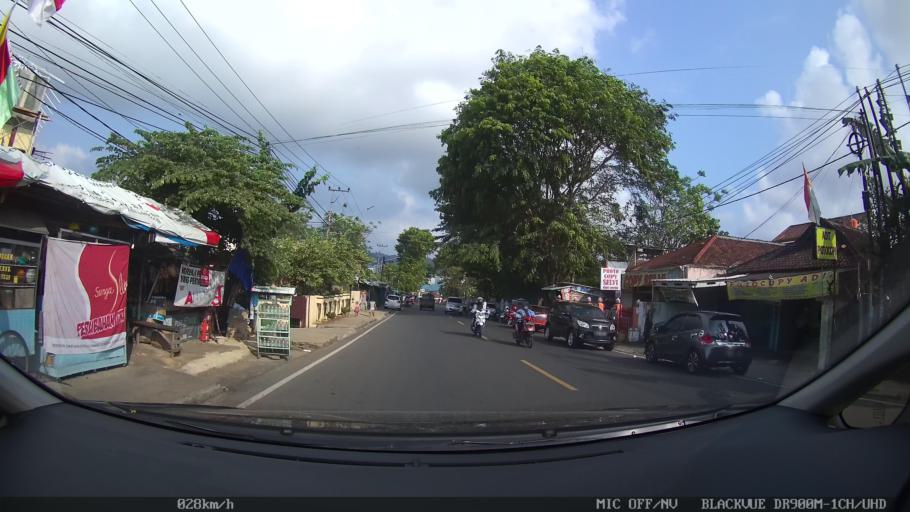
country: ID
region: Lampung
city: Bandarlampung
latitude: -5.4387
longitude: 105.2577
